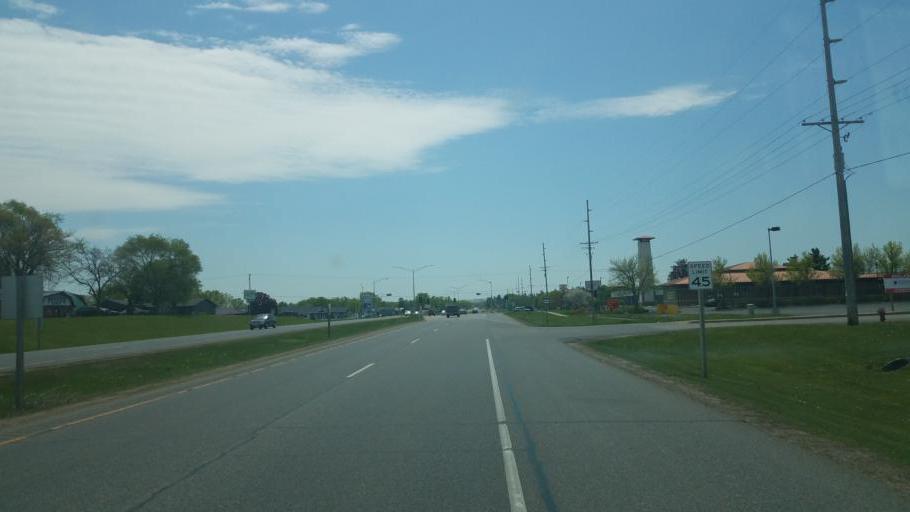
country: US
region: Wisconsin
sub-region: Monroe County
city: Tomah
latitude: 44.0028
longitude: -90.5050
